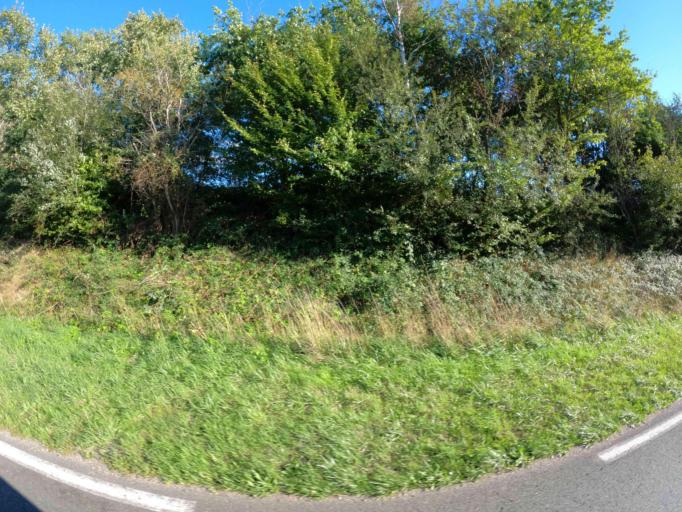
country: FR
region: Bourgogne
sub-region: Departement de Saone-et-Loire
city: Blanzy
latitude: 46.7095
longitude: 4.4177
